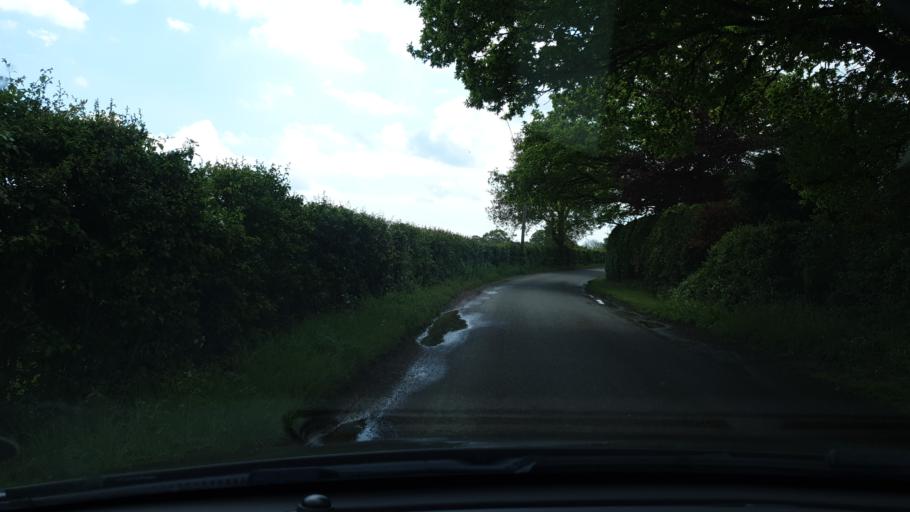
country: GB
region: England
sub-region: Essex
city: Great Bentley
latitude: 51.8756
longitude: 1.0608
